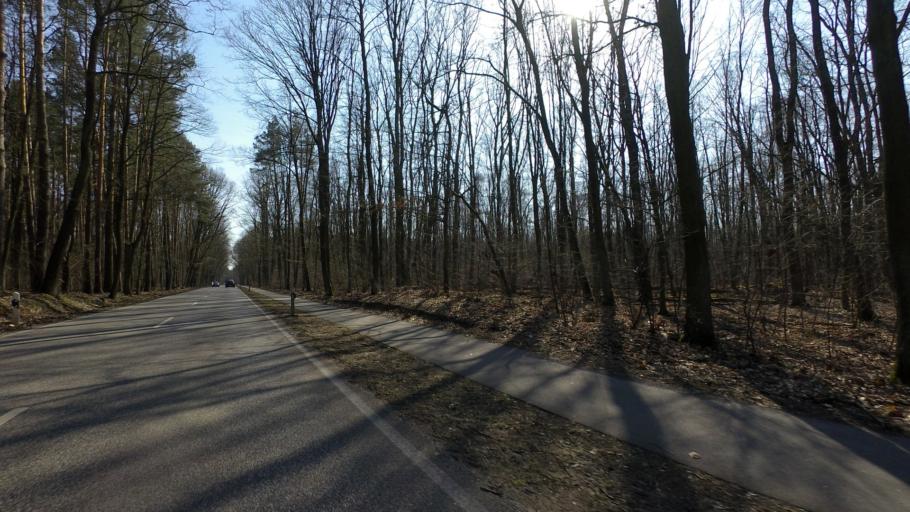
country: DE
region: Berlin
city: Konradshohe
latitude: 52.5945
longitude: 13.2029
